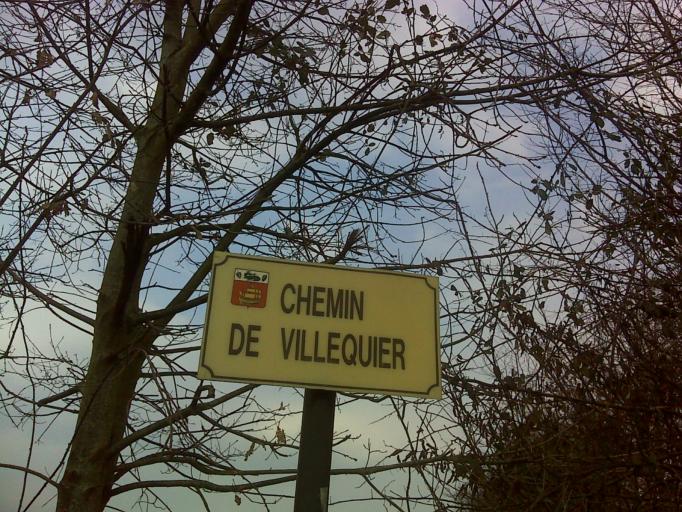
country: FR
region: Haute-Normandie
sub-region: Departement de la Seine-Maritime
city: Saint-Arnoult
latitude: 49.4990
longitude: 0.6963
